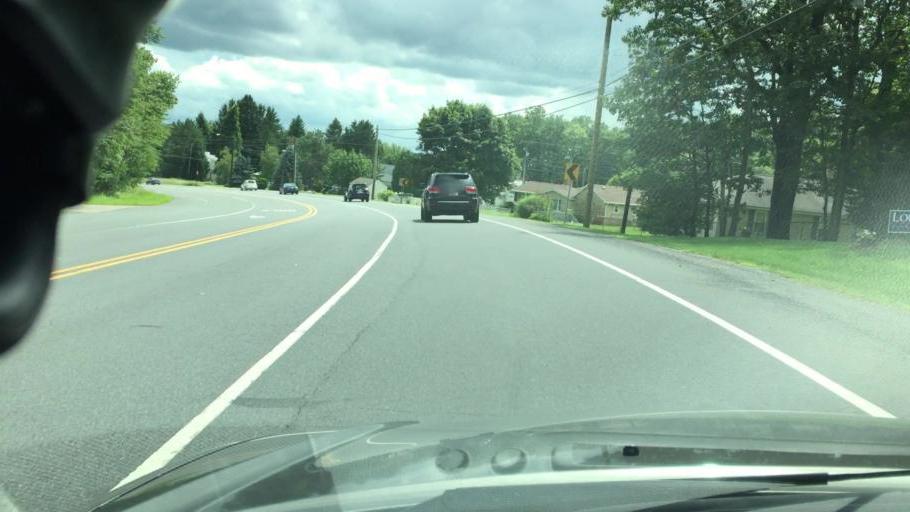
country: US
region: Pennsylvania
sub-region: Luzerne County
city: Harleigh
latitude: 40.9990
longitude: -75.9872
